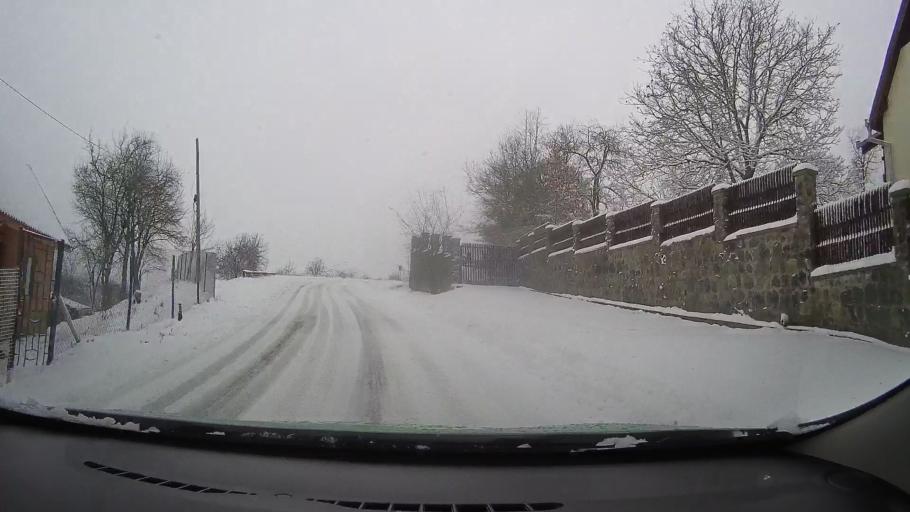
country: RO
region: Hunedoara
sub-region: Comuna Carjiti
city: Carjiti
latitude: 45.8463
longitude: 22.8634
